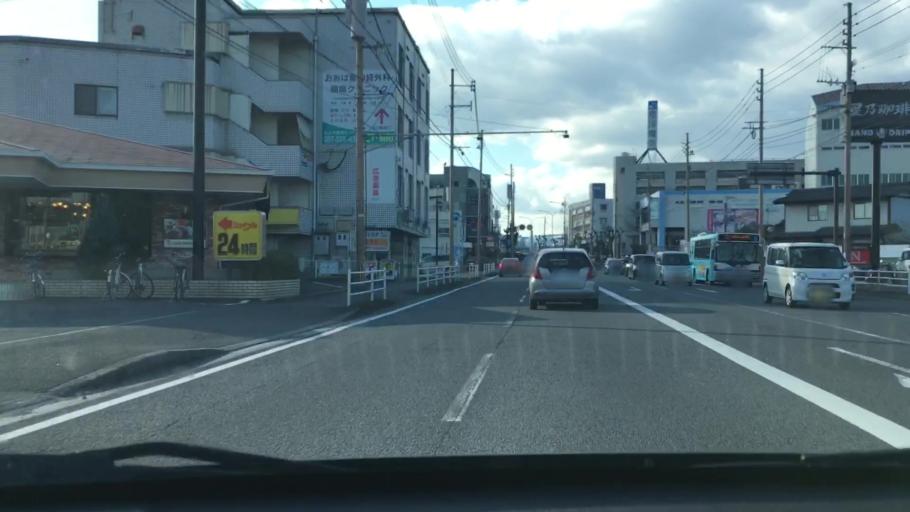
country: JP
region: Oita
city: Oita
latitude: 33.2318
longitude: 131.6287
